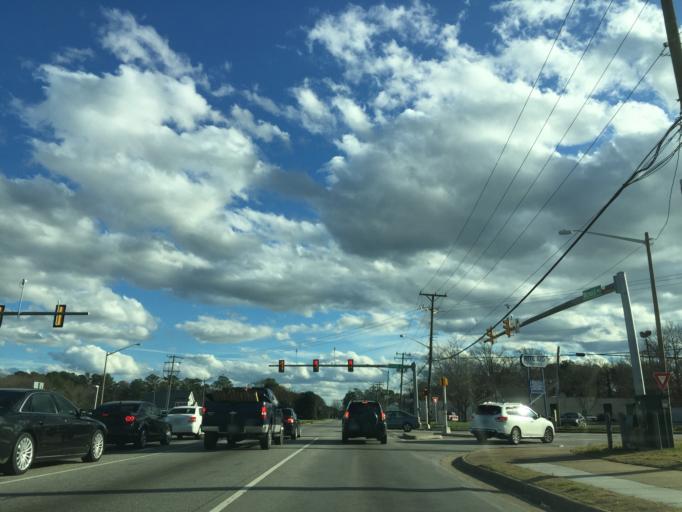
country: US
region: Virginia
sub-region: York County
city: Yorktown
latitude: 37.1142
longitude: -76.5195
